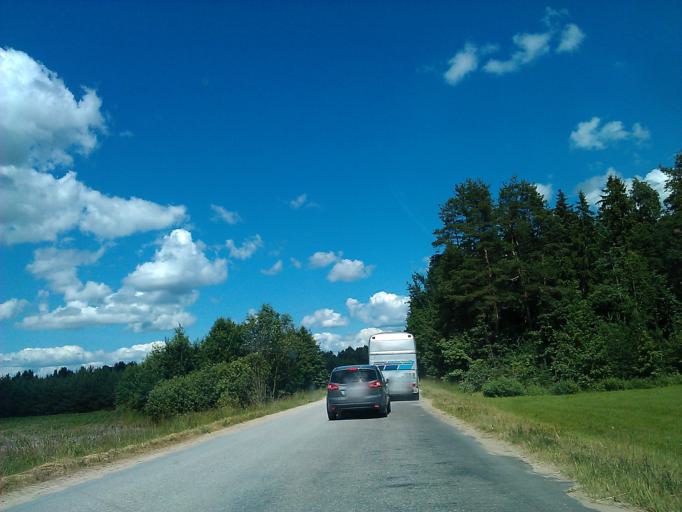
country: LV
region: Vilanu
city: Vilani
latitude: 56.5826
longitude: 26.9423
